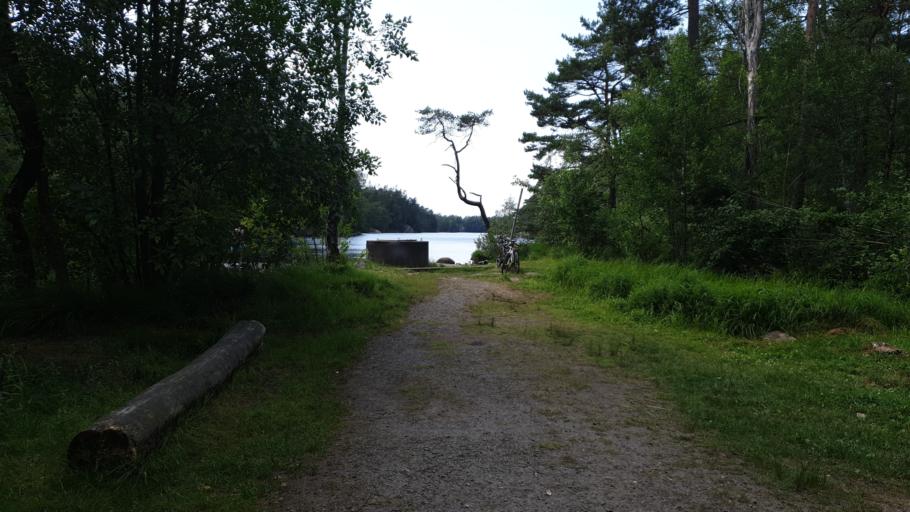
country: SE
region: Vaestra Goetaland
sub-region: Molndal
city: Moelndal
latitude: 57.6686
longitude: 12.0413
